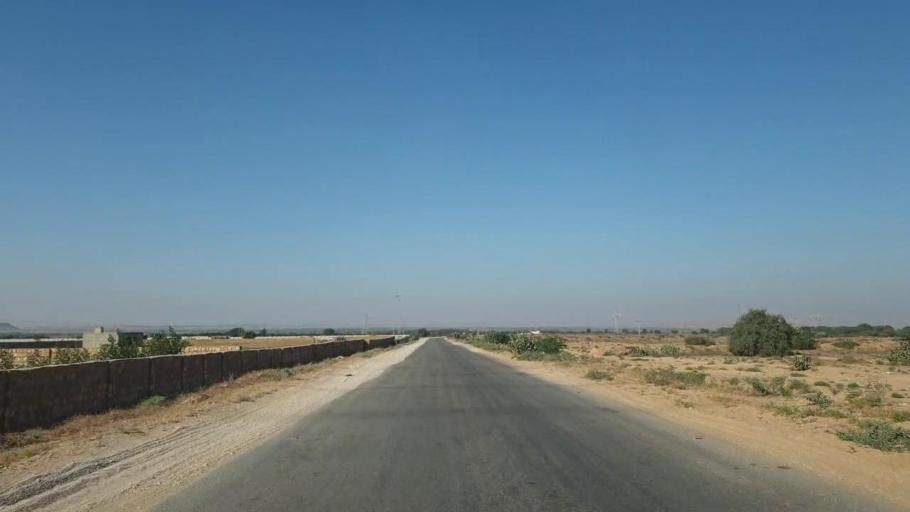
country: PK
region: Sindh
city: Gharo
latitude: 25.1811
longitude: 67.6583
